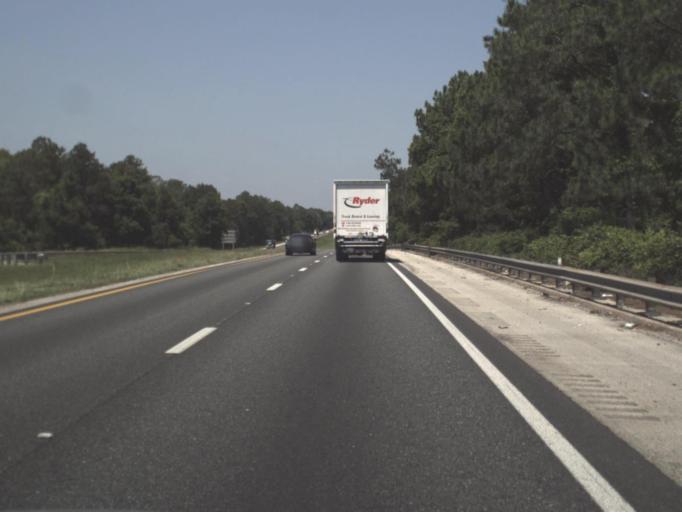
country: US
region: Florida
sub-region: Duval County
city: Baldwin
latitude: 30.3045
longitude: -81.8995
